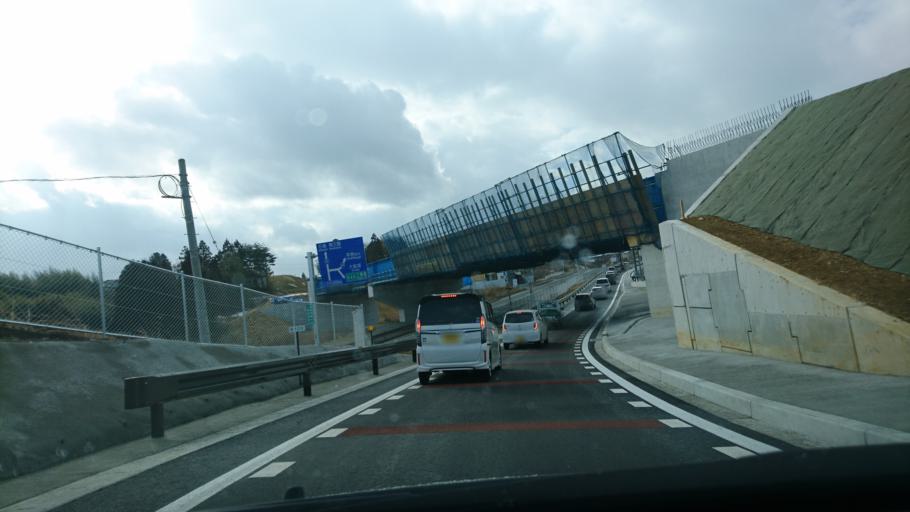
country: JP
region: Iwate
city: Ofunato
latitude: 38.7918
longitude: 141.5211
